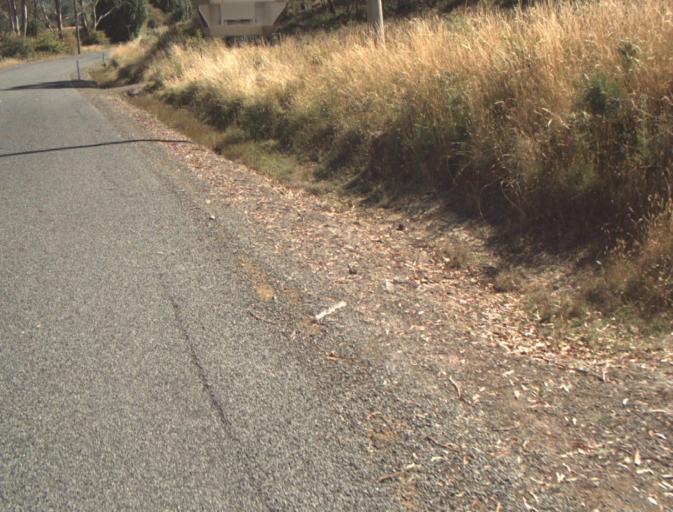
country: AU
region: Tasmania
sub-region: Launceston
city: Newstead
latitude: -41.3573
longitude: 147.3029
